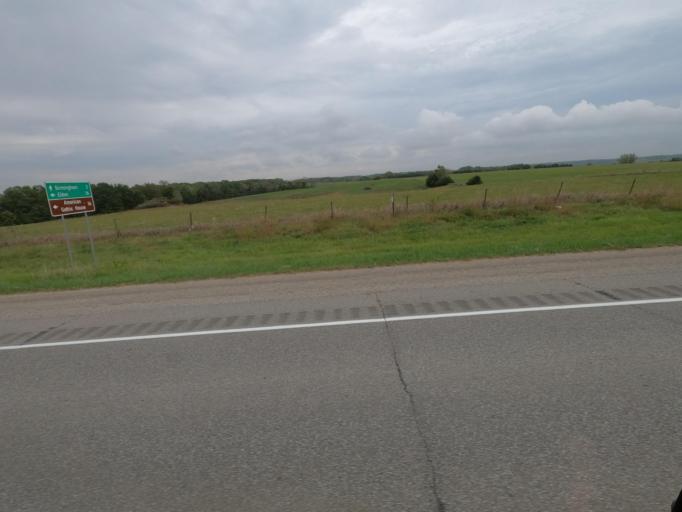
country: US
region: Iowa
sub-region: Van Buren County
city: Keosauqua
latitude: 40.8342
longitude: -91.9491
